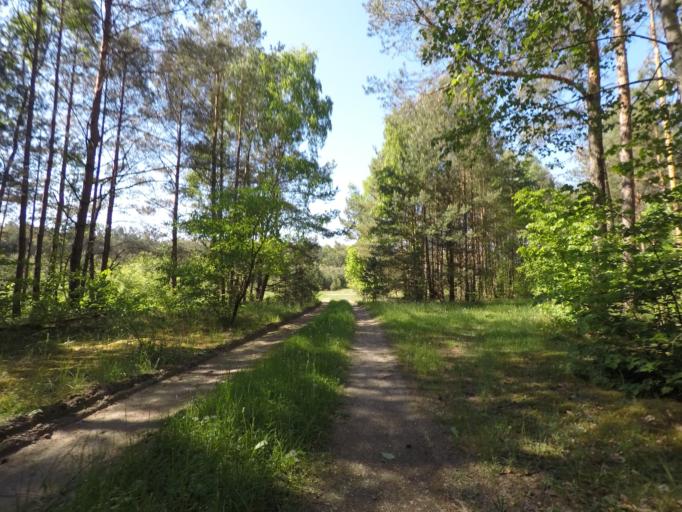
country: DE
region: Brandenburg
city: Melchow
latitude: 52.8238
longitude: 13.7493
